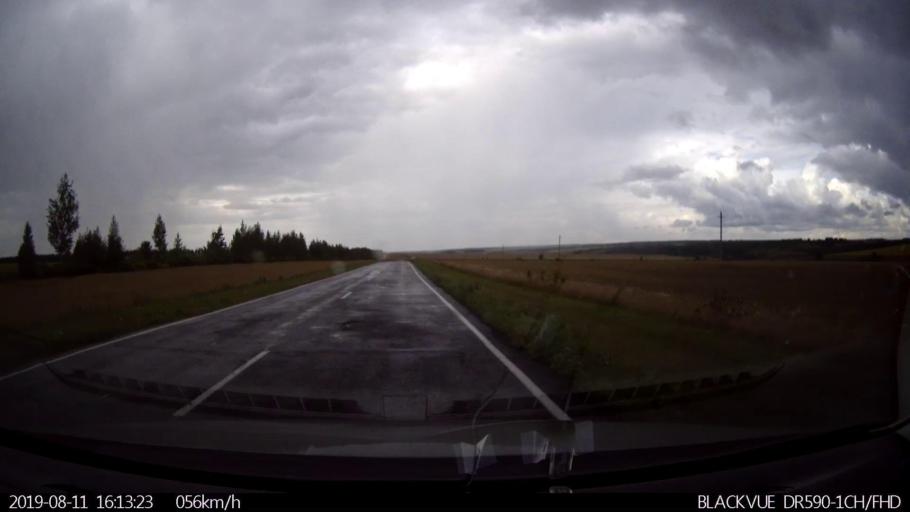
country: RU
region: Ulyanovsk
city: Ignatovka
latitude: 54.0197
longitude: 47.6371
